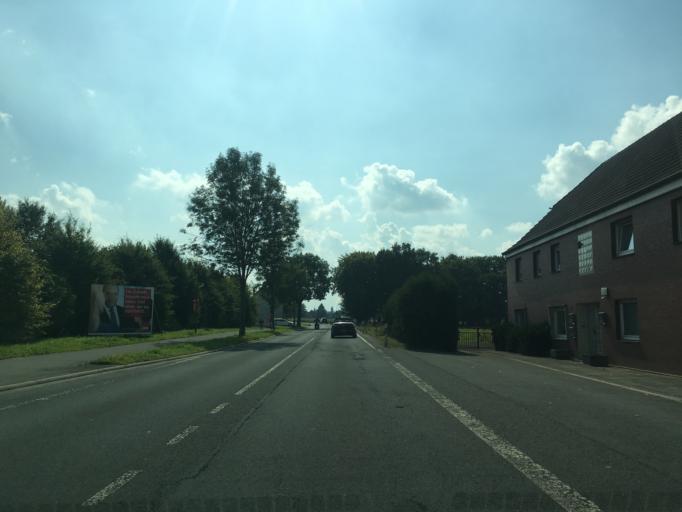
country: DE
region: North Rhine-Westphalia
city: Selm
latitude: 51.6798
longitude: 7.4707
